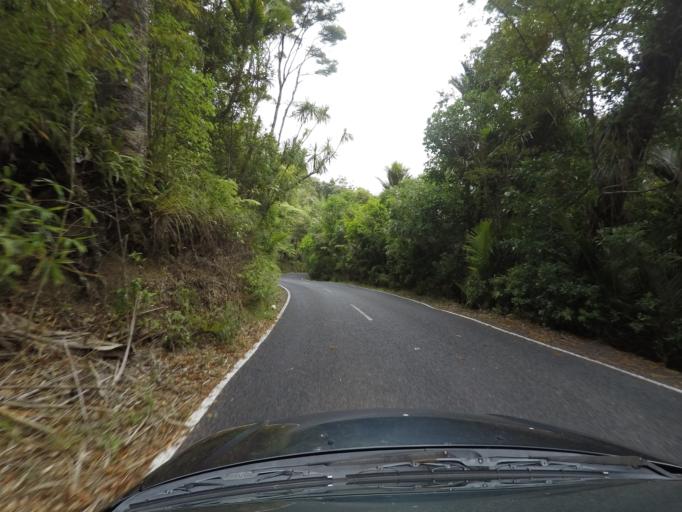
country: NZ
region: Auckland
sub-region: Auckland
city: Titirangi
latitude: -36.9462
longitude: 174.6590
